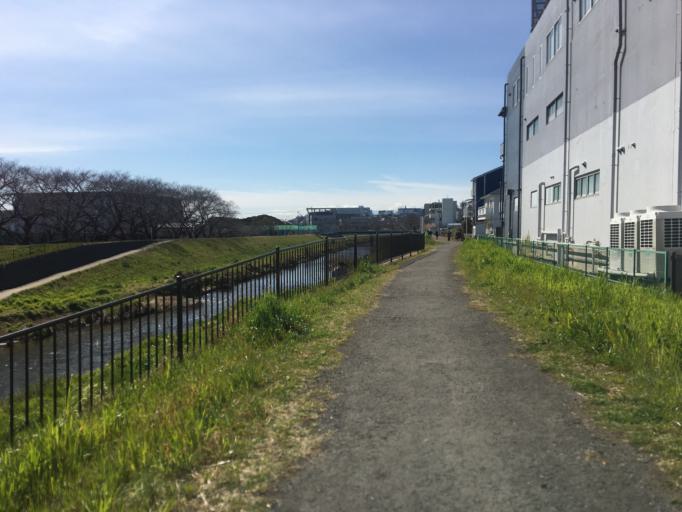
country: JP
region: Saitama
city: Asaka
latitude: 35.8165
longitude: 139.5941
